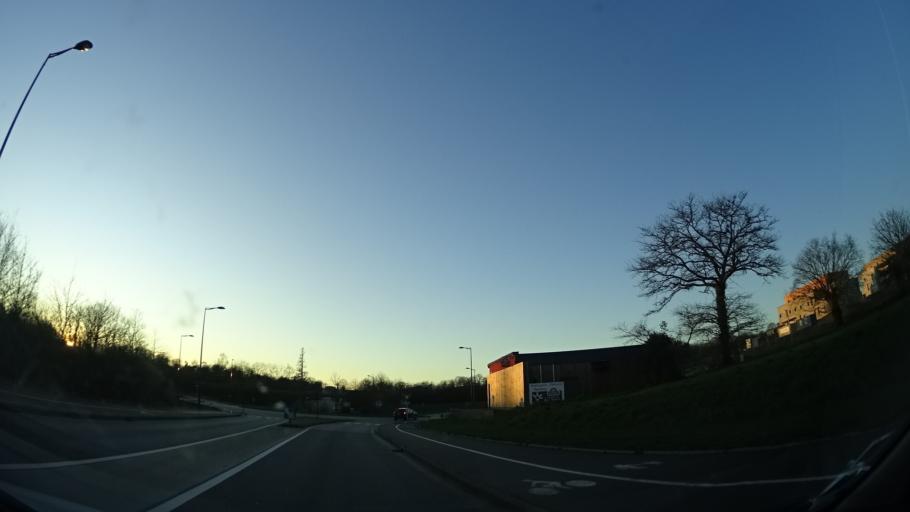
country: FR
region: Brittany
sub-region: Departement d'Ille-et-Vilaine
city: Poce-les-Bois
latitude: 48.1225
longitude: -1.2309
